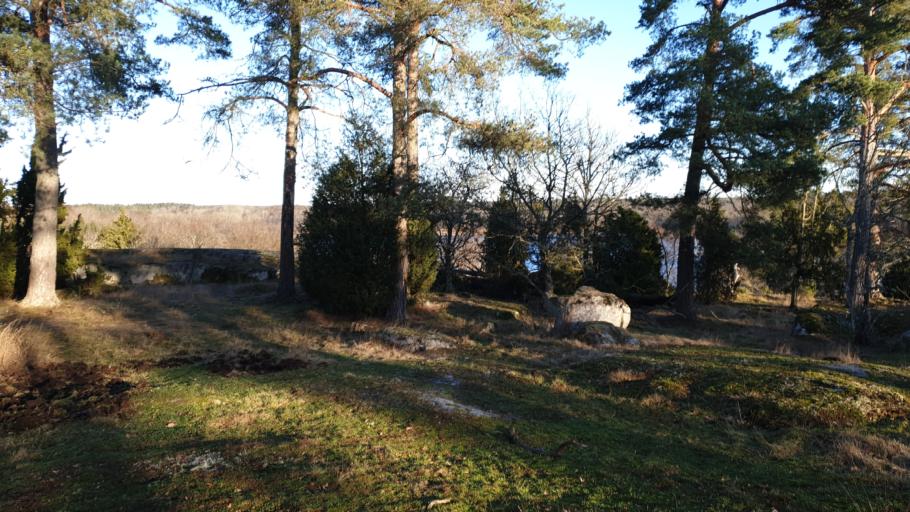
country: SE
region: Blekinge
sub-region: Ronneby Kommun
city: Brakne-Hoby
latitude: 56.2330
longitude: 15.1829
